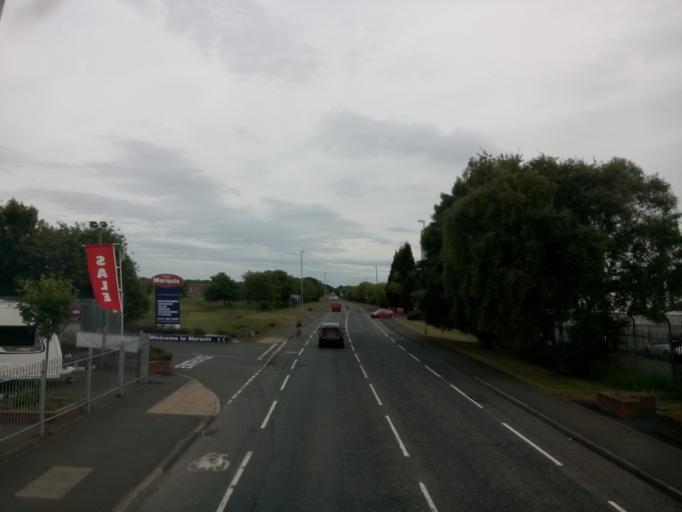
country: GB
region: England
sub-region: County Durham
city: Chester-le-Street
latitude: 54.8879
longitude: -1.5765
